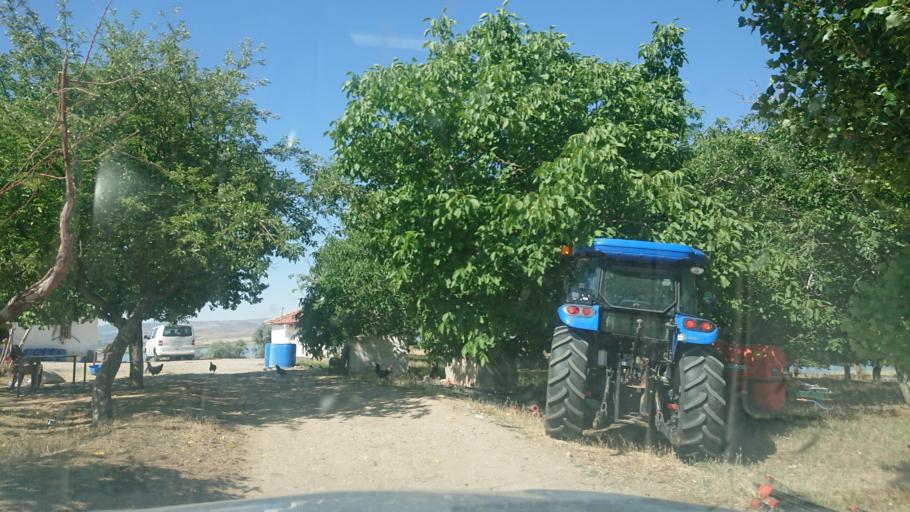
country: TR
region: Ankara
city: Evren
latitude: 39.0516
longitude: 33.8768
